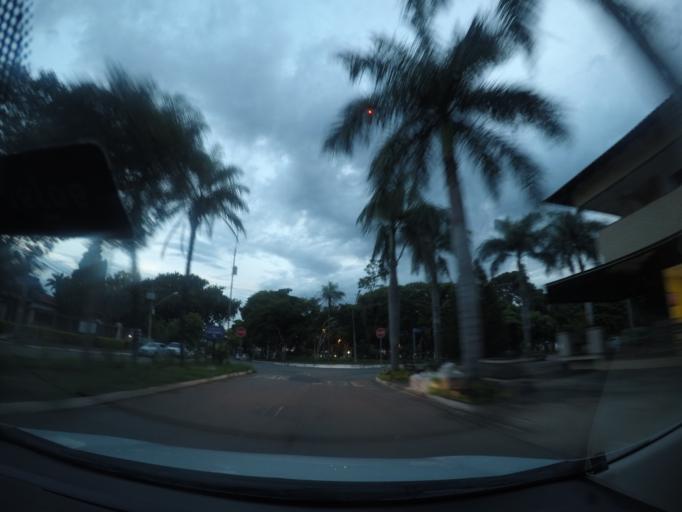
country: BR
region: Goias
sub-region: Goiania
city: Goiania
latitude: -16.6494
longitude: -49.2282
